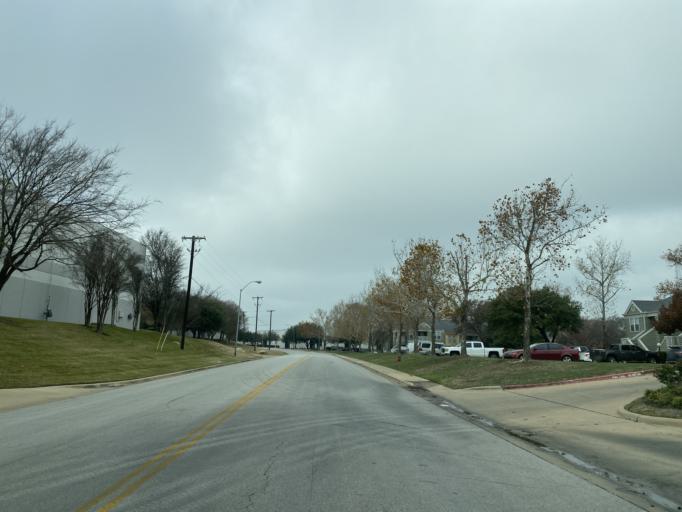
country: US
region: Texas
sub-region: Williamson County
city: Round Rock
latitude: 30.5368
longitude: -97.6826
